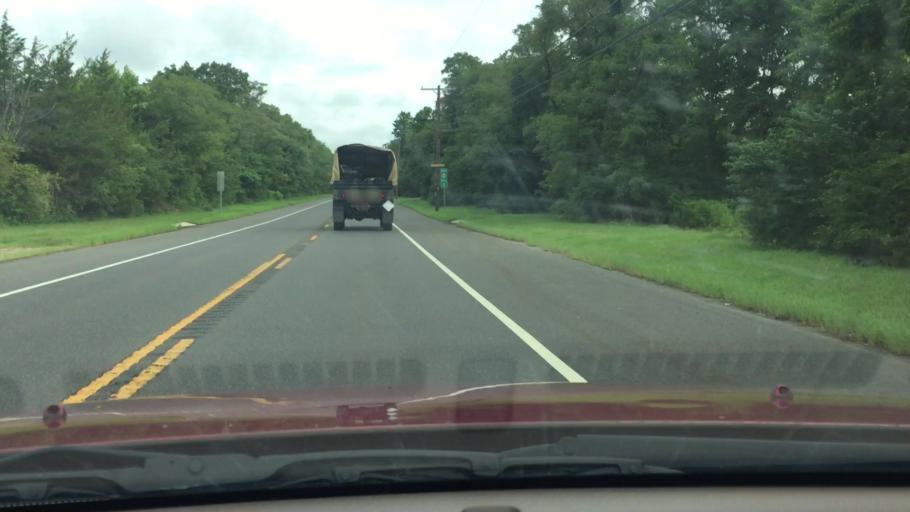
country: US
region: New Jersey
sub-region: Burlington County
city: Fort Dix
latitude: 40.0446
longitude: -74.6459
